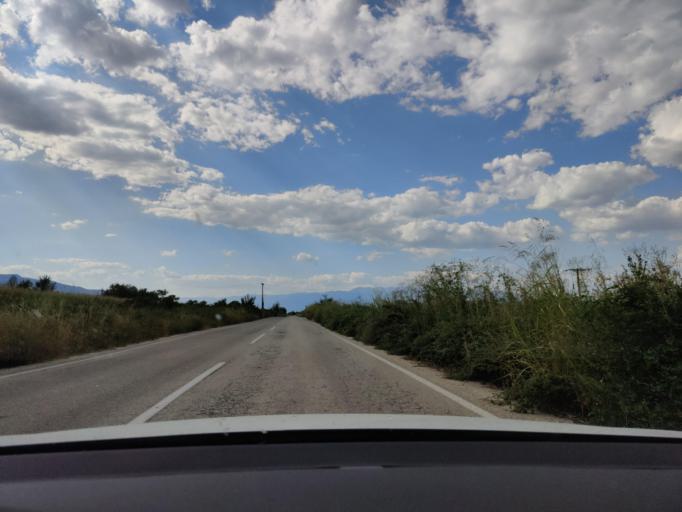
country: GR
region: Central Macedonia
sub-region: Nomos Serron
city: Strymoniko
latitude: 41.0744
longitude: 23.2978
